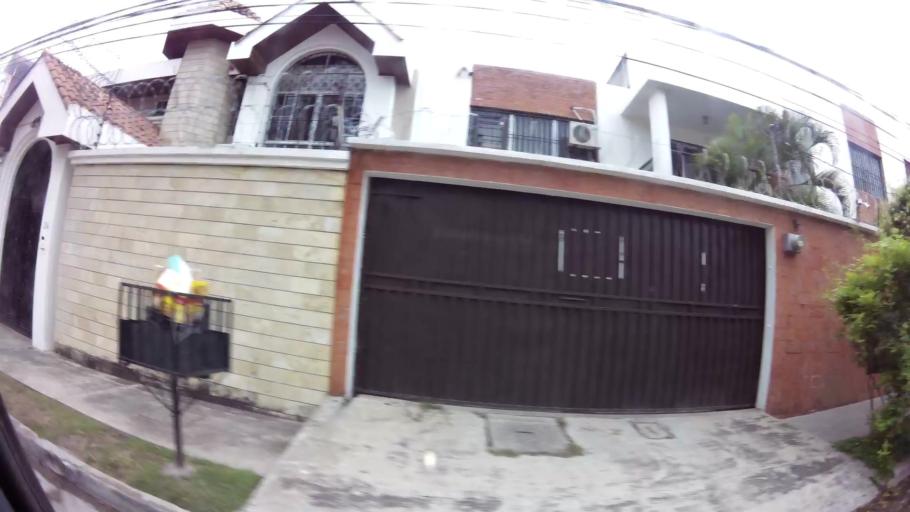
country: HN
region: Francisco Morazan
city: Tegucigalpa
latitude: 14.0953
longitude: -87.1725
